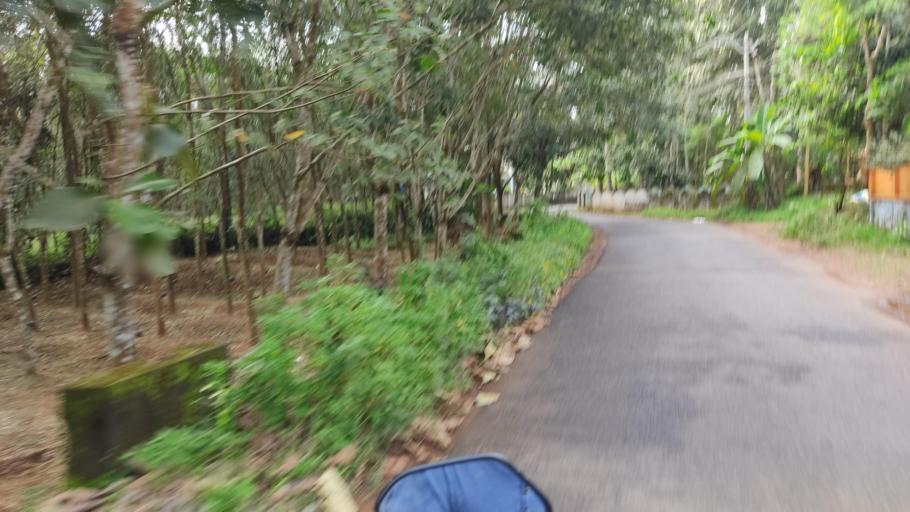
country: IN
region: Kerala
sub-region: Pattanamtitta
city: Adur
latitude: 9.1964
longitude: 76.7783
